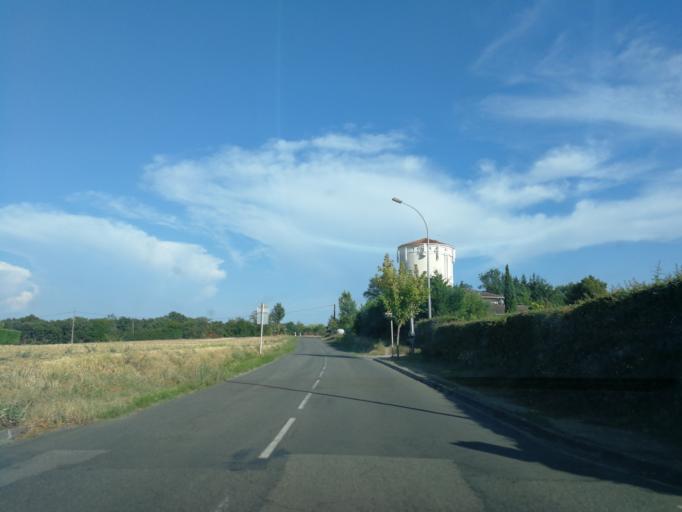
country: FR
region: Midi-Pyrenees
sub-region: Departement de la Haute-Garonne
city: Balma
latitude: 43.6167
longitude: 1.5213
